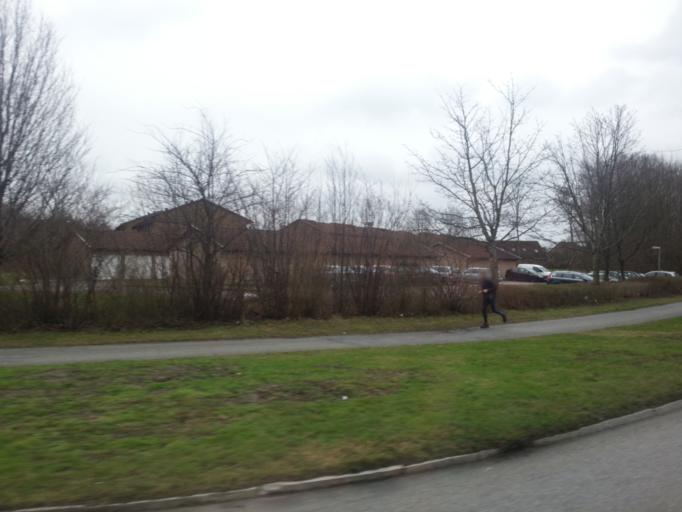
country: SE
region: Skane
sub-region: Lunds Kommun
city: Lund
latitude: 55.7223
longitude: 13.1580
